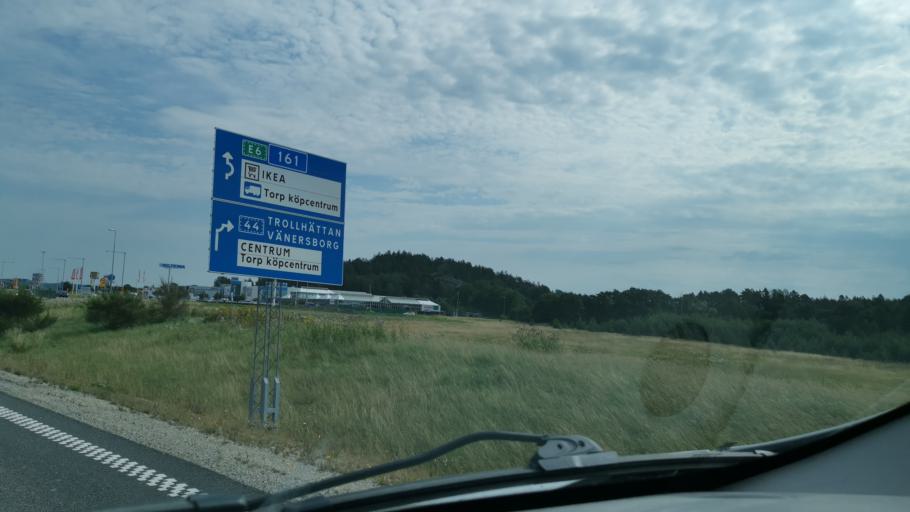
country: SE
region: Vaestra Goetaland
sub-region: Uddevalla Kommun
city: Uddevalla
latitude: 58.3495
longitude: 11.7977
